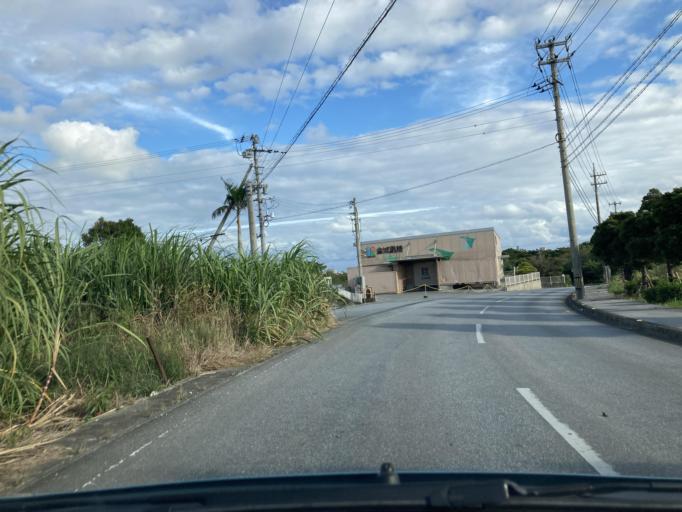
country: JP
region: Okinawa
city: Itoman
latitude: 26.1351
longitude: 127.7495
